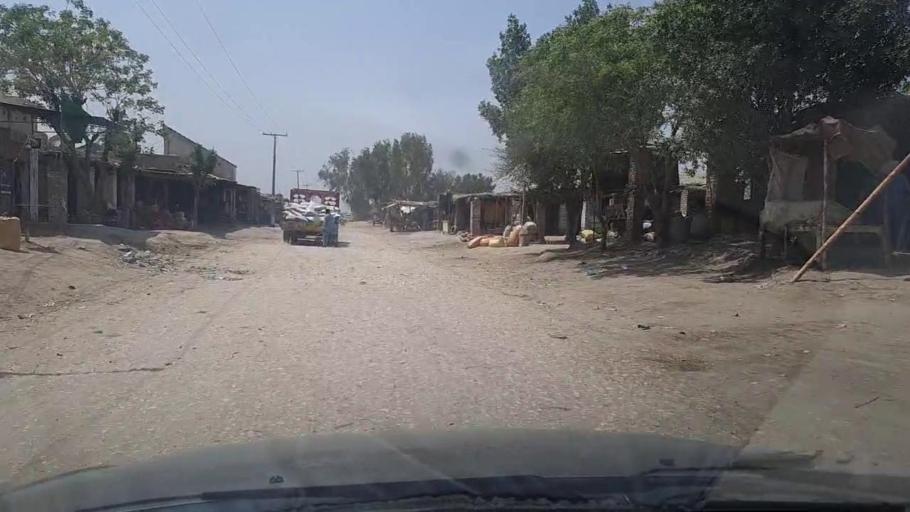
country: PK
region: Sindh
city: Bhiria
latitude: 26.8901
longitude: 68.2625
